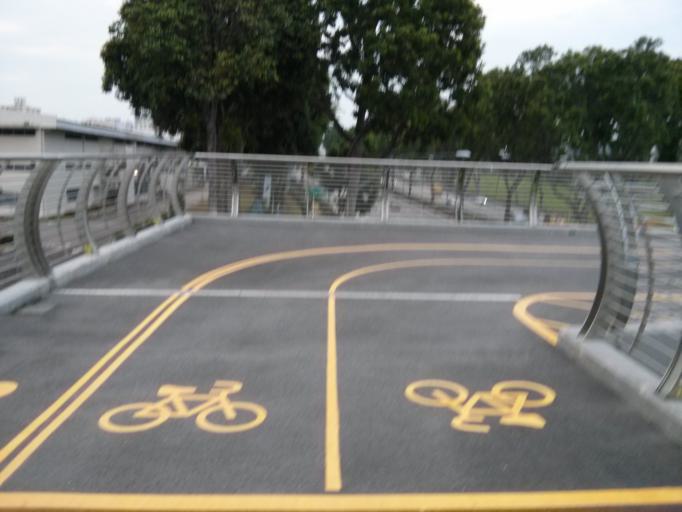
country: SG
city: Singapore
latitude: 1.3220
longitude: 103.7508
